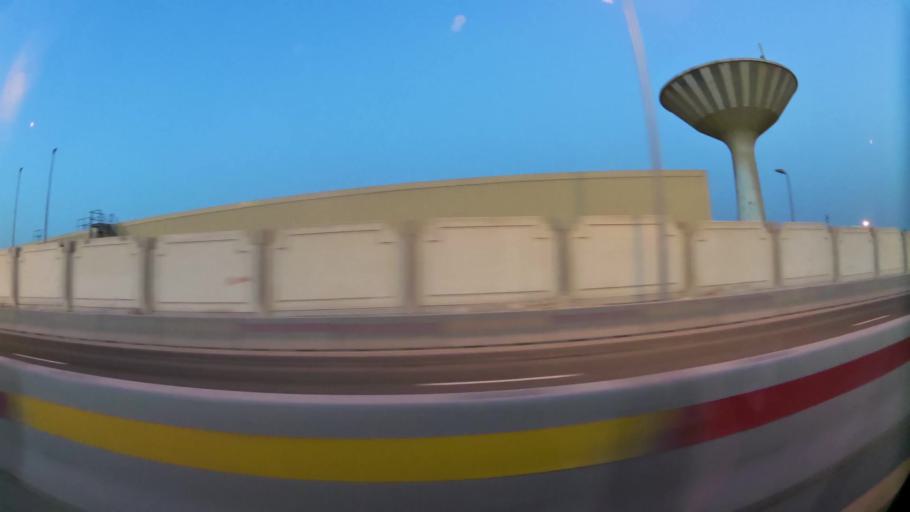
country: QA
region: Baladiyat ar Rayyan
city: Ar Rayyan
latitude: 25.3151
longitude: 51.4510
